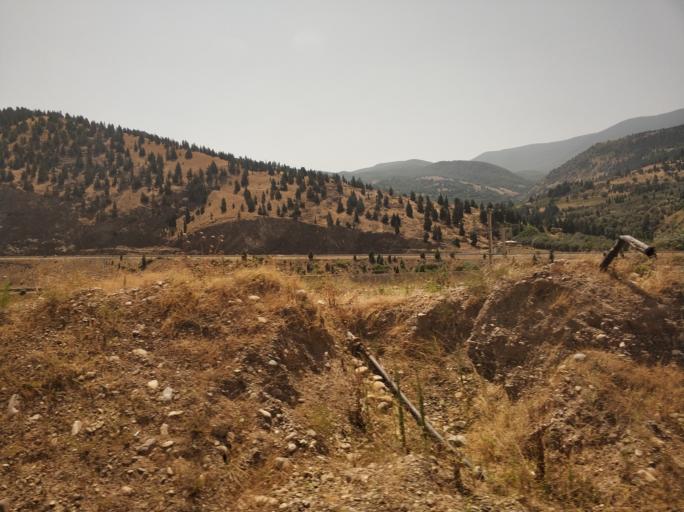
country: IR
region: Gilan
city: Pa'in-e Bazar-e Rudbar
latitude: 36.8502
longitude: 49.4755
